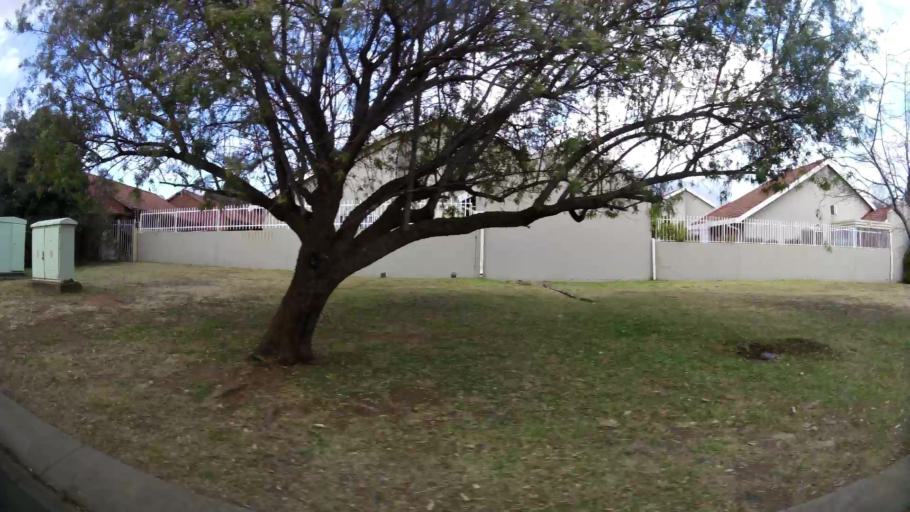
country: ZA
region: Orange Free State
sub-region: Mangaung Metropolitan Municipality
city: Bloemfontein
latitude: -29.0764
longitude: 26.1941
